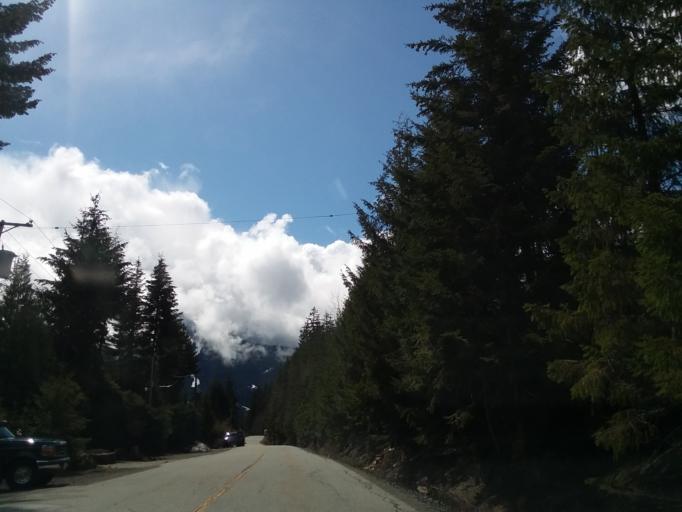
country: CA
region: British Columbia
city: Whistler
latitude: 50.1189
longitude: -122.9864
